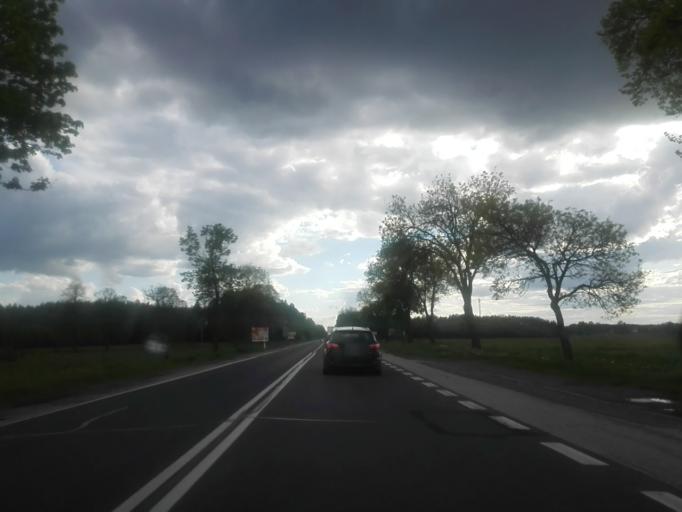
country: PL
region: Masovian Voivodeship
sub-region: Powiat ostrowski
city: Brok
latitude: 52.7565
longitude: 21.7939
